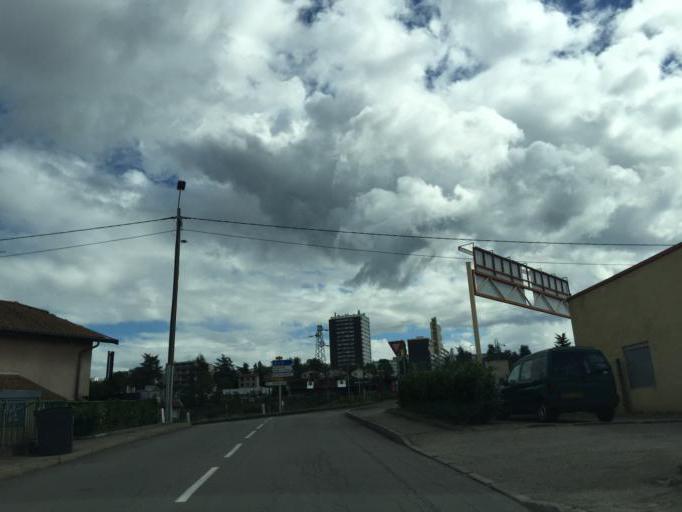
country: FR
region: Rhone-Alpes
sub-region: Departement de la Loire
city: Lorette
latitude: 45.5211
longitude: 4.5926
